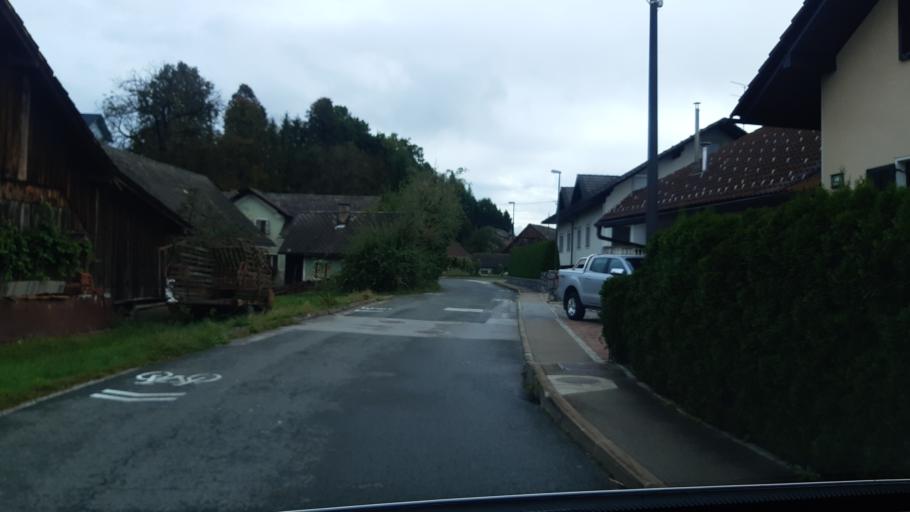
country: SI
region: Vodice
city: Vodice
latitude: 46.1908
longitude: 14.4948
